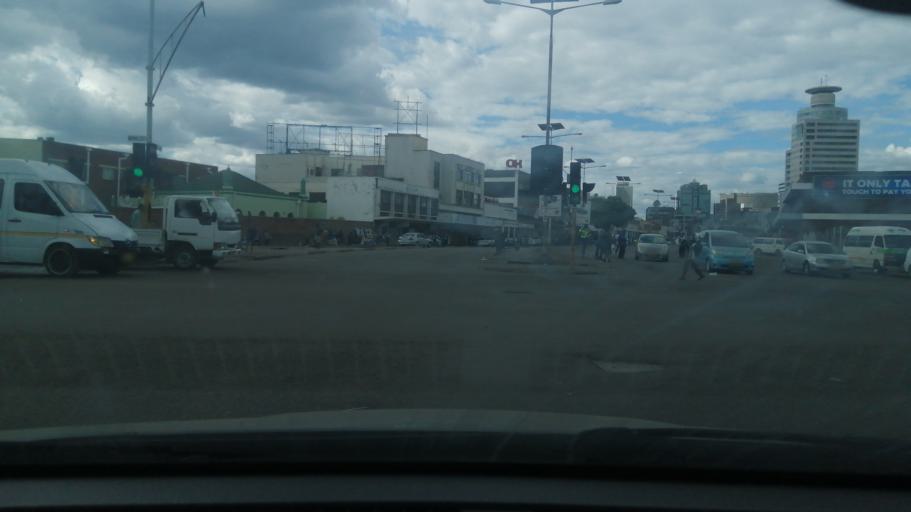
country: ZW
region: Harare
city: Harare
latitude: -17.8362
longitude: 31.0467
